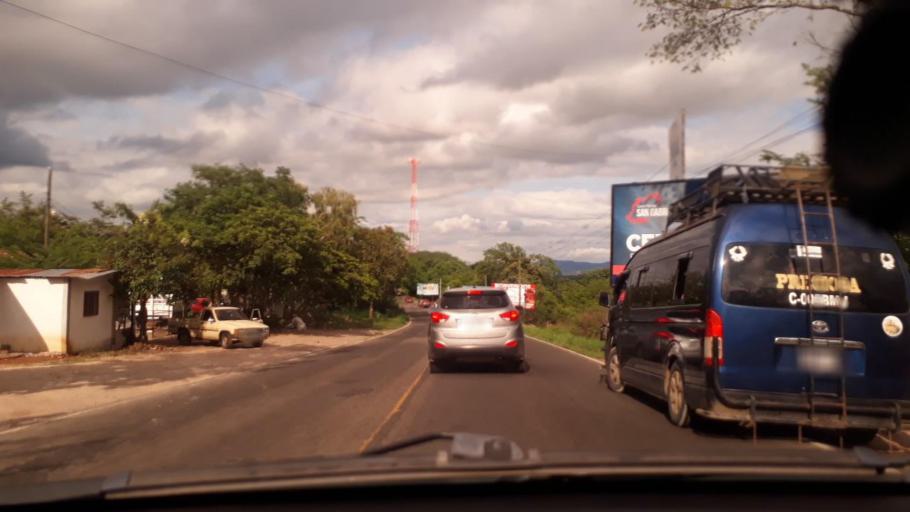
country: GT
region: Jutiapa
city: Quesada
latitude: 14.2751
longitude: -89.9748
